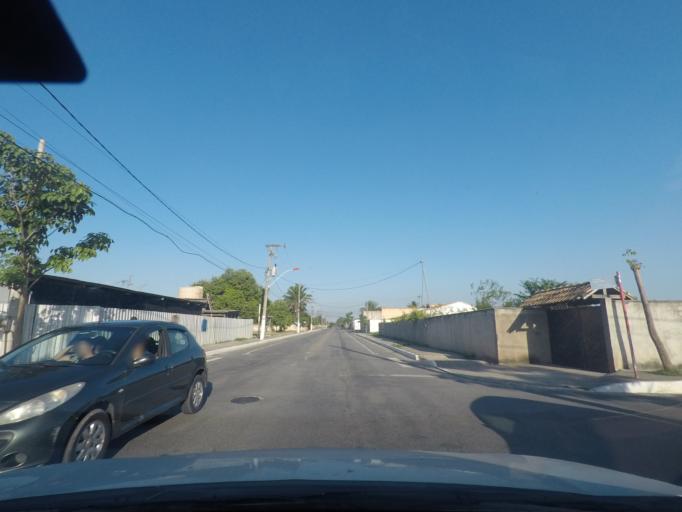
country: BR
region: Rio de Janeiro
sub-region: Marica
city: Marica
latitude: -22.9566
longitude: -42.9362
